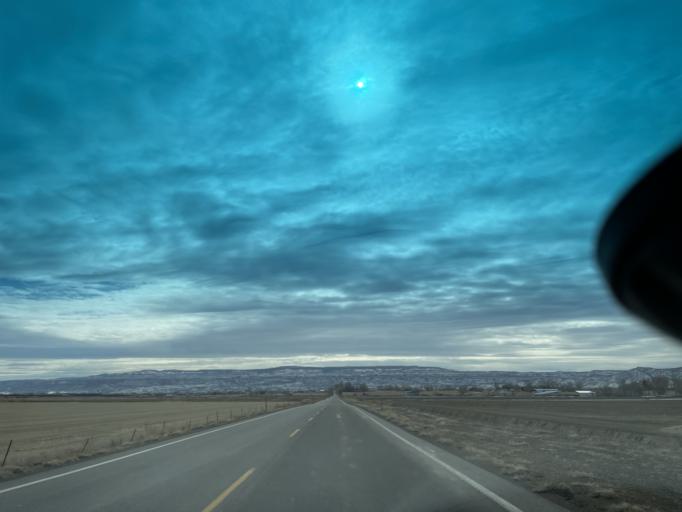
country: US
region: Colorado
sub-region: Mesa County
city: Loma
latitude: 39.2357
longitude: -108.8130
